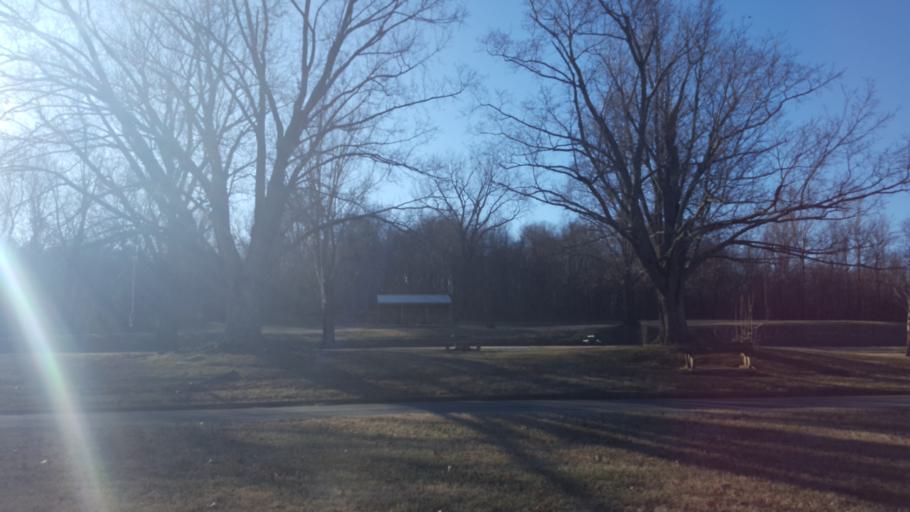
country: US
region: Kentucky
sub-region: Crittenden County
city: Marion
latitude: 37.4660
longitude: -88.0932
